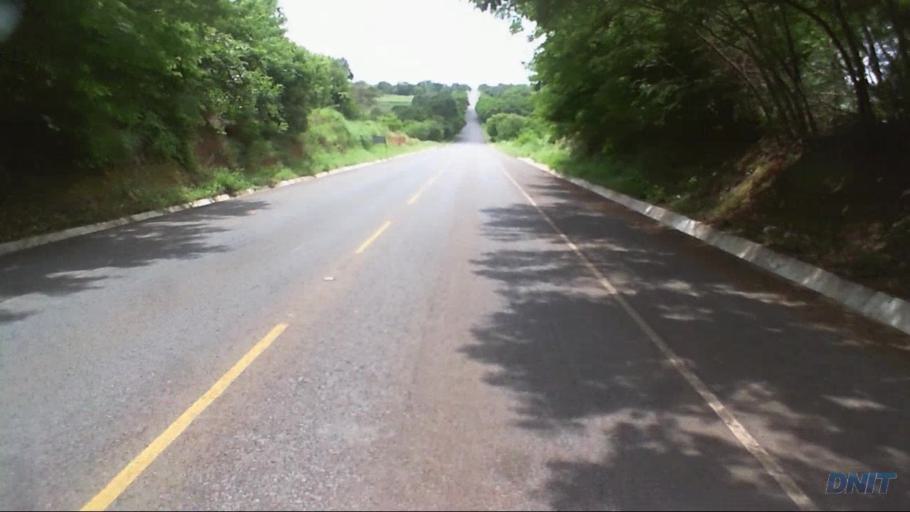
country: BR
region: Goias
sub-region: Sao Miguel Do Araguaia
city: Sao Miguel do Araguaia
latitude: -13.2865
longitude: -50.1936
